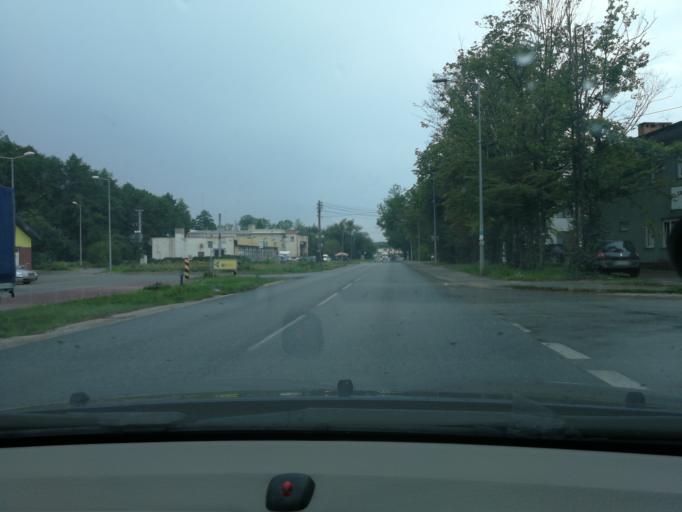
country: PL
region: Masovian Voivodeship
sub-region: Powiat zyrardowski
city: Radziejowice
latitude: 52.0024
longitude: 20.5584
